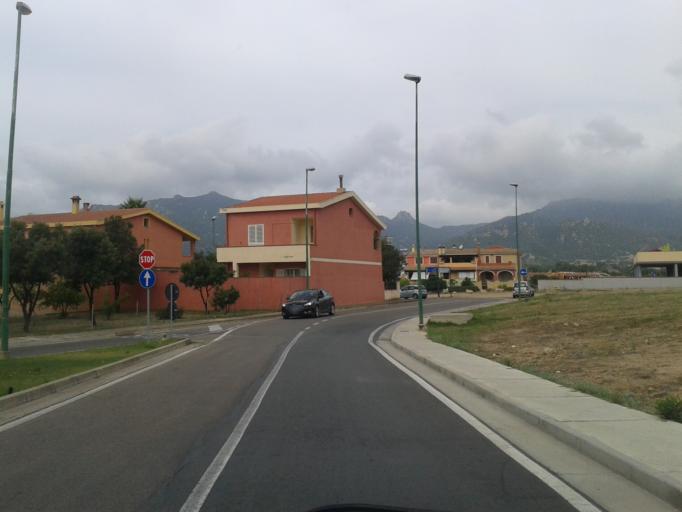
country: IT
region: Sardinia
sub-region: Provincia di Cagliari
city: Villasimius
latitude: 39.1483
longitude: 9.5174
